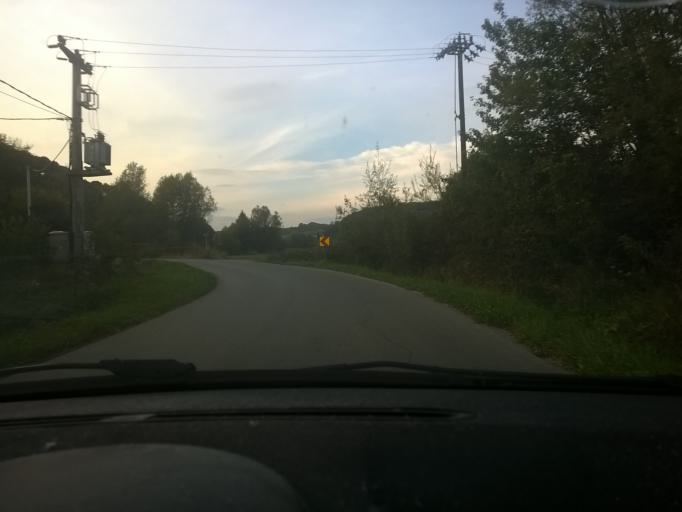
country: HR
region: Krapinsko-Zagorska
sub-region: Grad Krapina
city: Krapina
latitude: 46.1176
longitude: 15.8608
